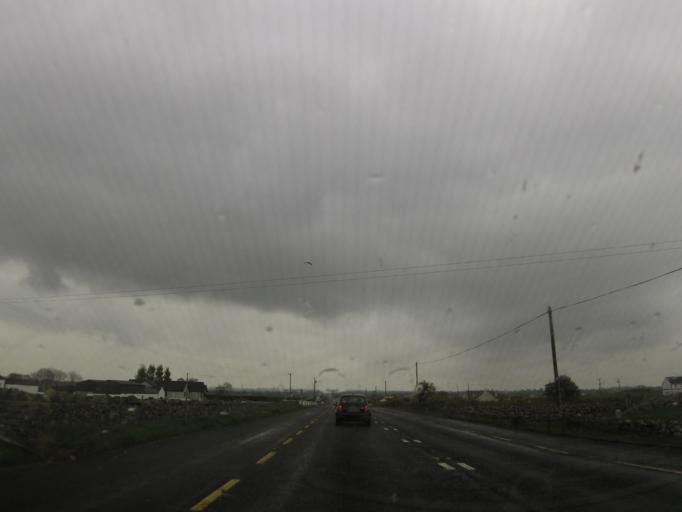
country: IE
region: Connaught
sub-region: County Galway
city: Tuam
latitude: 53.4749
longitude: -8.9094
